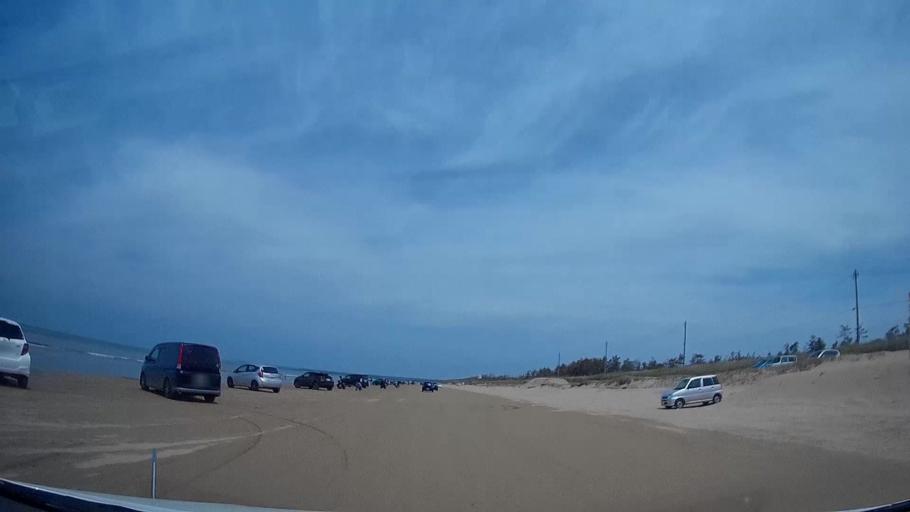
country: JP
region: Ishikawa
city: Hakui
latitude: 36.8420
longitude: 136.7502
